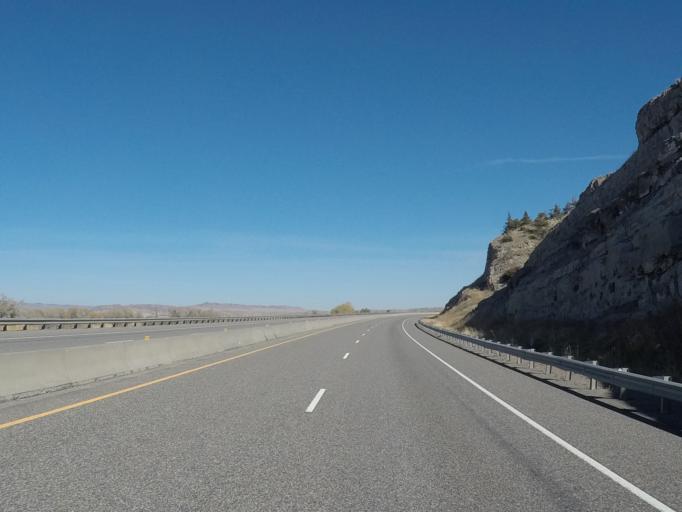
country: US
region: Montana
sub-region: Sweet Grass County
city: Big Timber
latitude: 45.7310
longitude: -110.2348
